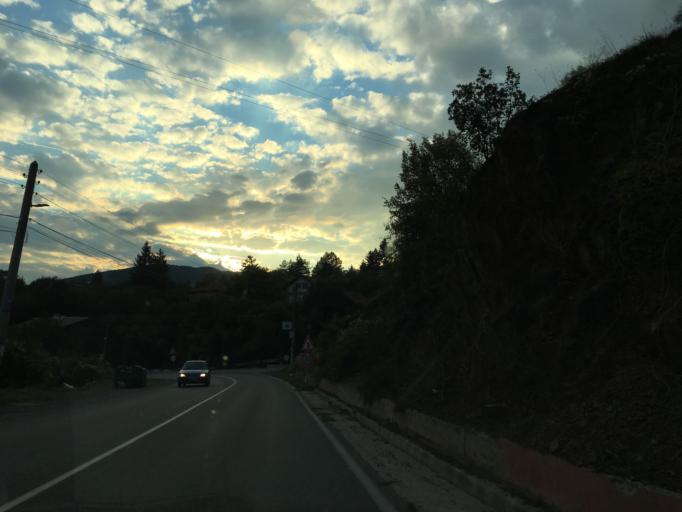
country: BG
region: Sofiya
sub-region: Obshtina Svoge
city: Svoge
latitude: 42.8685
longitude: 23.3708
